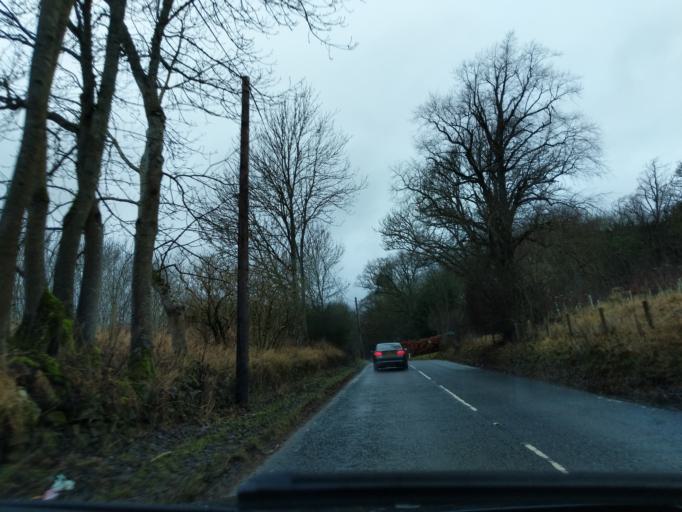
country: GB
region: Scotland
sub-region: The Scottish Borders
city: Galashiels
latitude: 55.6438
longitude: -2.8496
